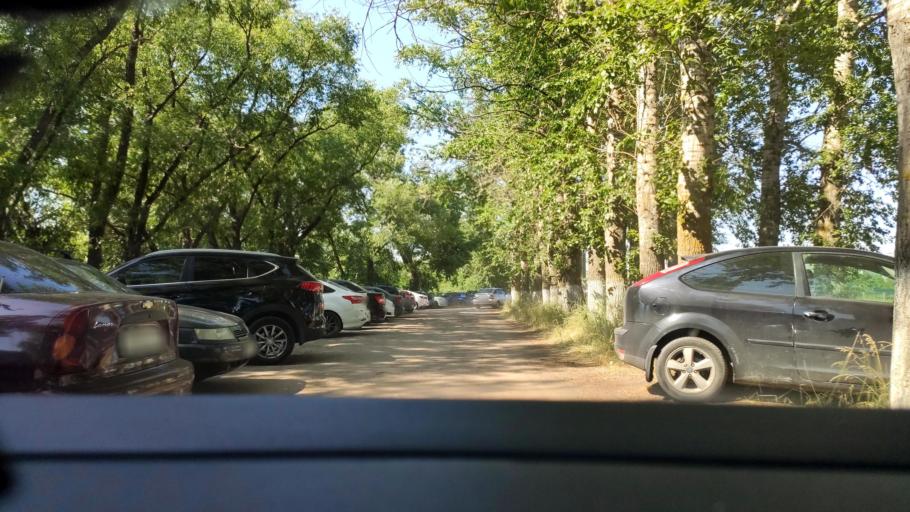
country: RU
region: Voronezj
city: Novaya Usman'
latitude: 51.6360
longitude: 39.4112
